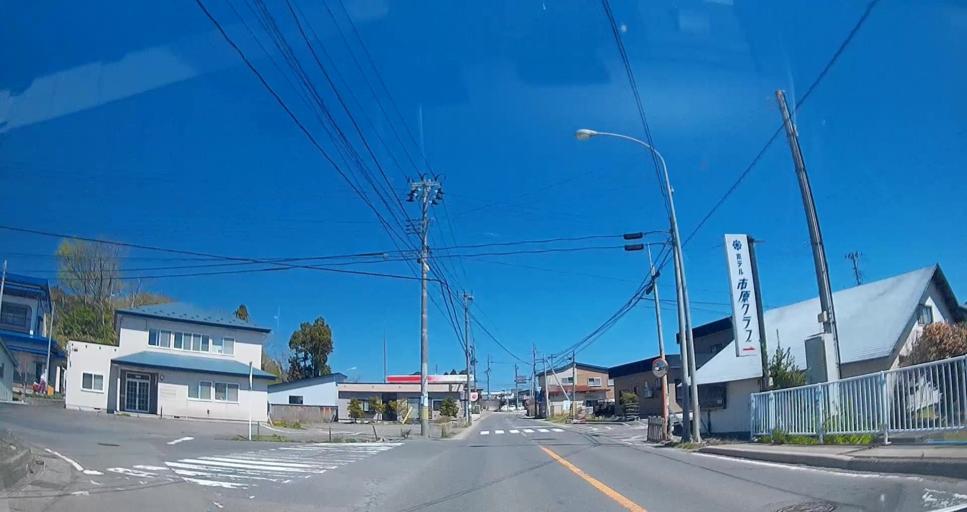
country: JP
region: Aomori
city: Misawa
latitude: 40.9613
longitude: 141.3733
